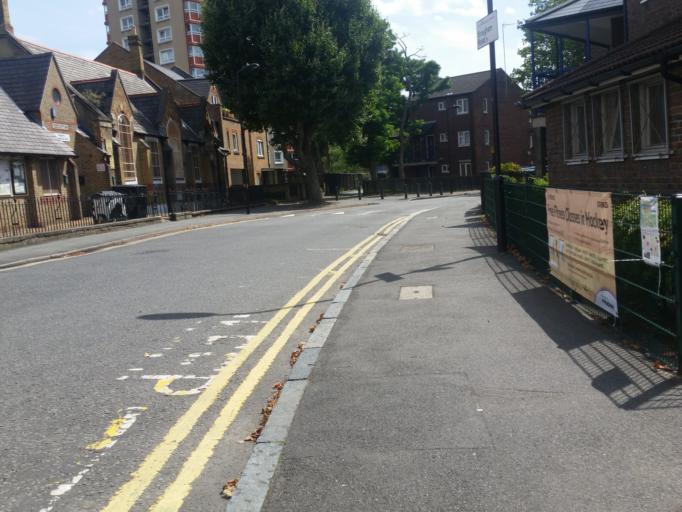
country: GB
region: England
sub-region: Greater London
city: Bethnal Green
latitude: 51.5375
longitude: -0.0638
